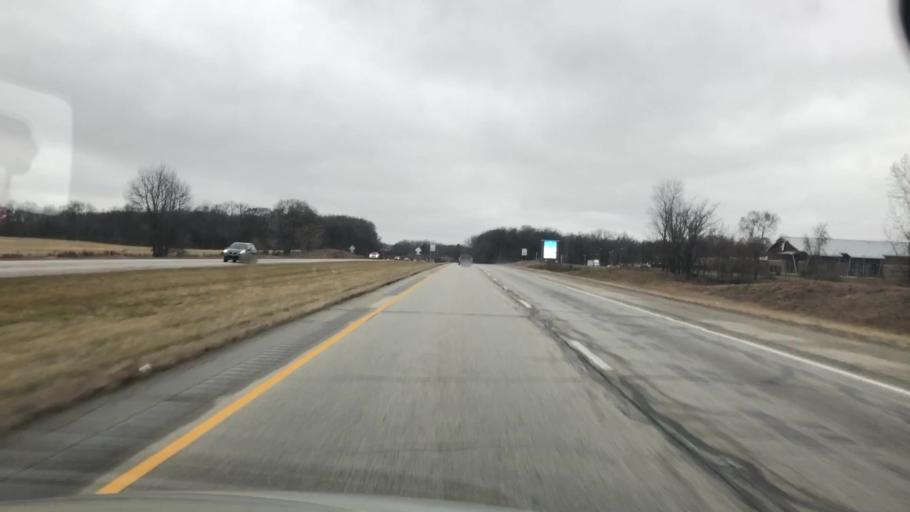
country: US
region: Indiana
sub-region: Kosciusko County
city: Winona Lake
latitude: 41.2543
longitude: -85.8296
